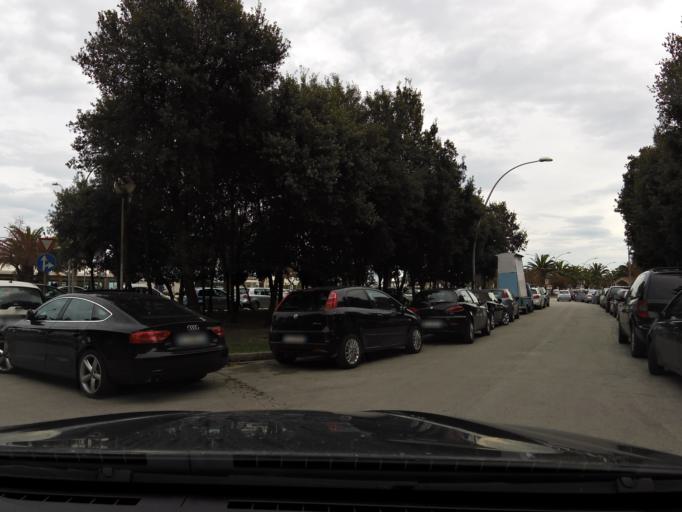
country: IT
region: The Marches
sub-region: Provincia di Macerata
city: Portocivitanova
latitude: 43.3090
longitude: 13.7329
